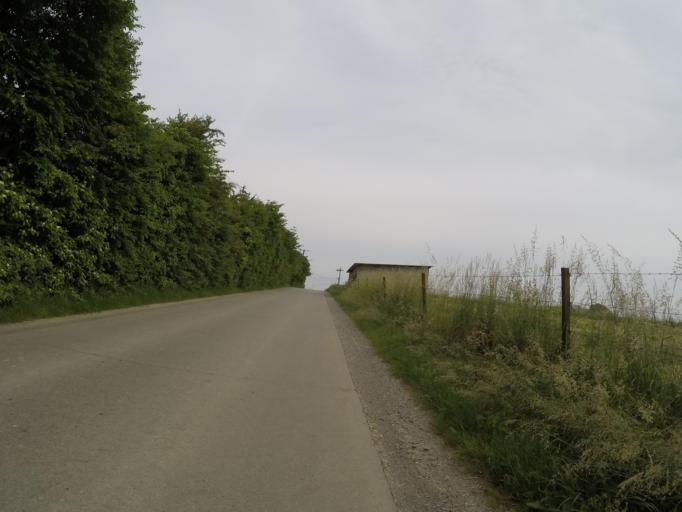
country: BE
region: Wallonia
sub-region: Province de Namur
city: Dinant
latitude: 50.2912
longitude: 4.9596
